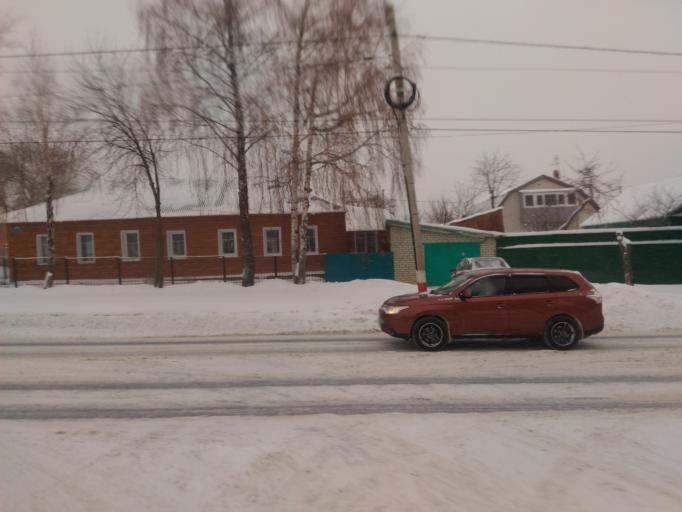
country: RU
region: Ulyanovsk
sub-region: Ulyanovskiy Rayon
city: Ulyanovsk
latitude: 54.3506
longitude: 48.3822
